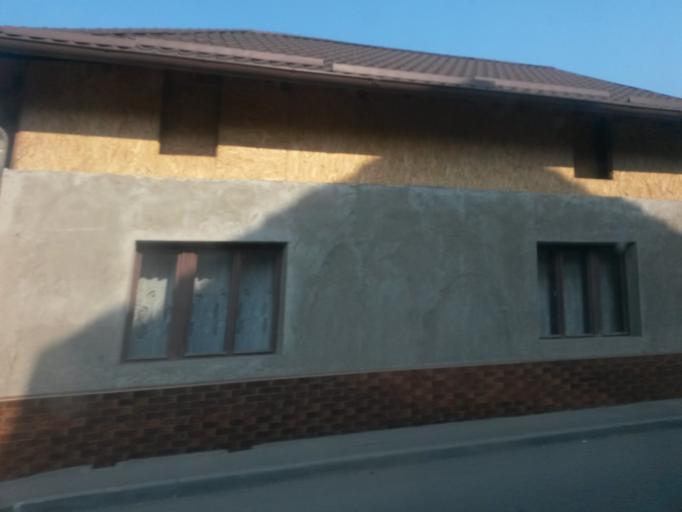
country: RO
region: Cluj
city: Turda
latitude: 46.5714
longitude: 23.7799
